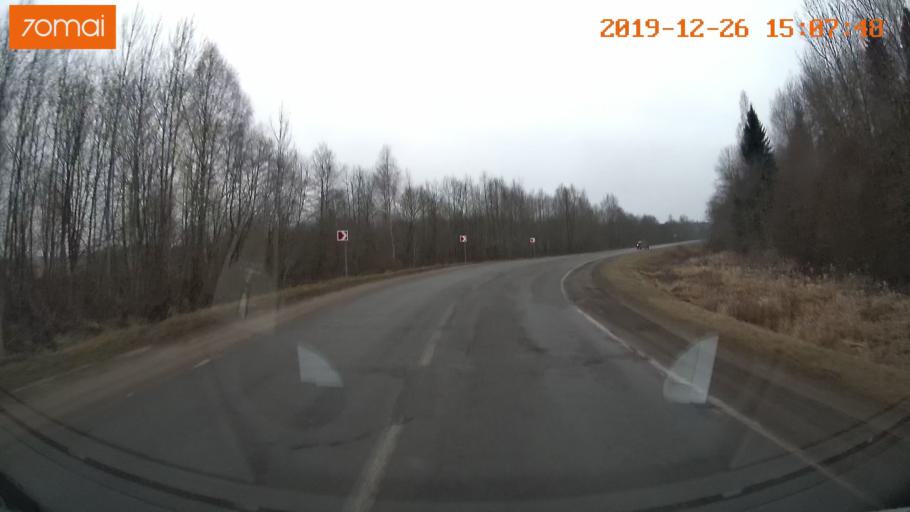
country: RU
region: Jaroslavl
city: Rybinsk
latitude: 58.1662
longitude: 38.8423
